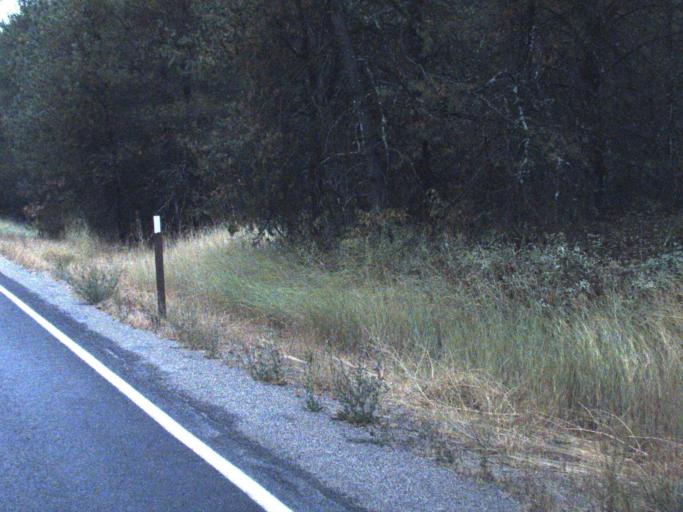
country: US
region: Washington
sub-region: Stevens County
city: Chewelah
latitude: 48.0424
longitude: -117.7385
